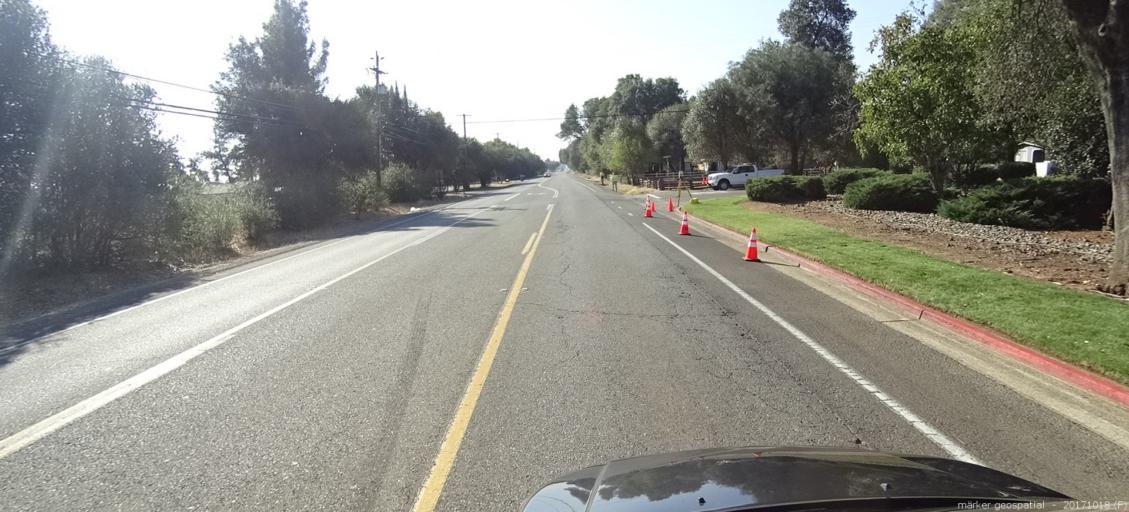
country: US
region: California
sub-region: Shasta County
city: Palo Cedro
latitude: 40.5434
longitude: -122.3028
